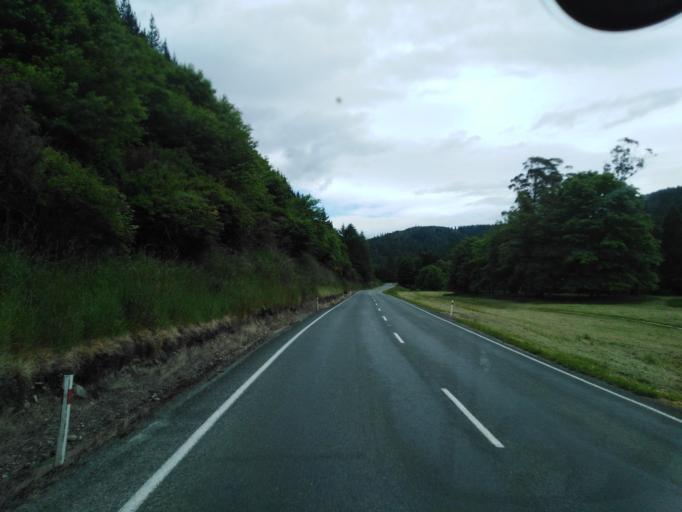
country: NZ
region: Tasman
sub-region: Tasman District
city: Wakefield
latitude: -41.4820
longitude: 172.8793
